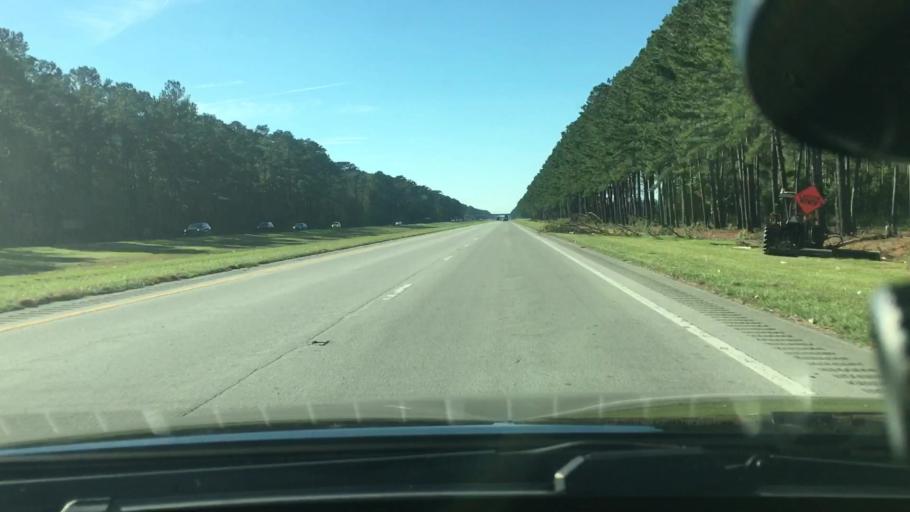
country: US
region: North Carolina
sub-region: Craven County
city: Trent Woods
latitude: 35.1226
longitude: -77.1190
